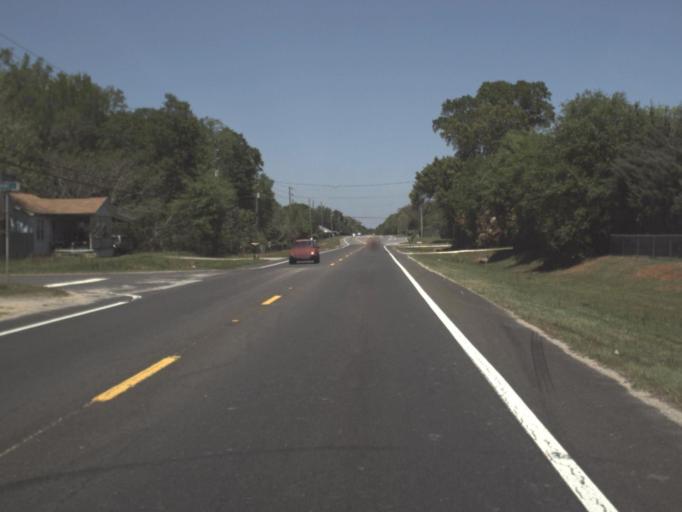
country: US
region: Florida
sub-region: Escambia County
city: Bellview
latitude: 30.4744
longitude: -87.3237
